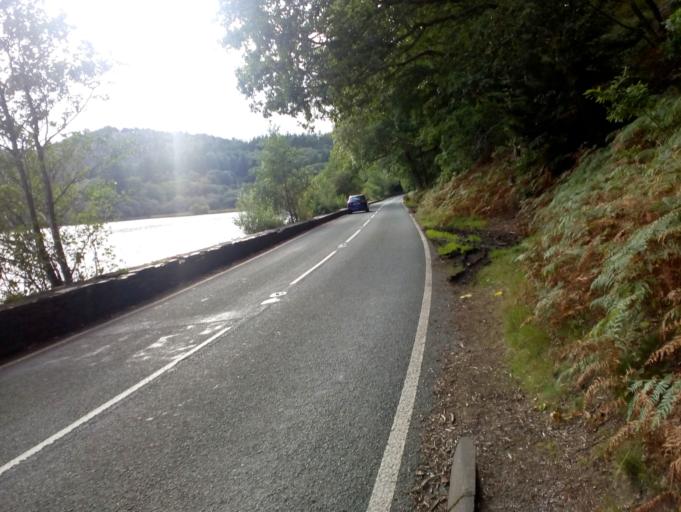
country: GB
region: Wales
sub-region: Gwynedd
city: Maentwrog
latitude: 52.9521
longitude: -4.0048
